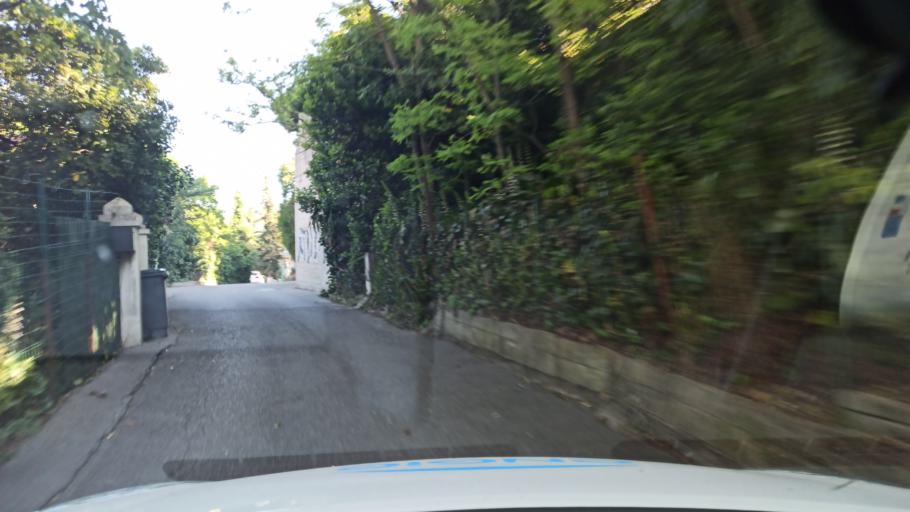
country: FR
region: Languedoc-Roussillon
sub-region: Departement du Gard
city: Villeneuve-les-Avignon
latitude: 43.9515
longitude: 4.7840
